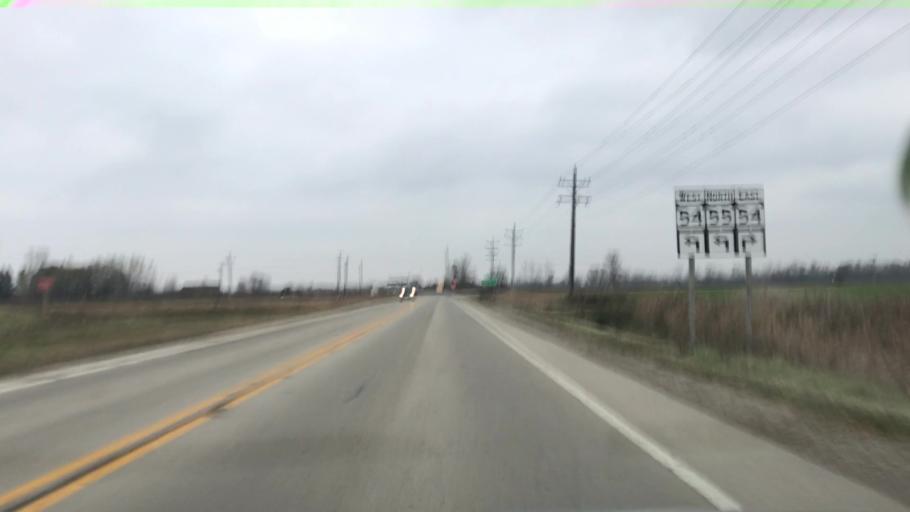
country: US
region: Wisconsin
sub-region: Outagamie County
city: Seymour
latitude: 44.4980
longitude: -88.2912
